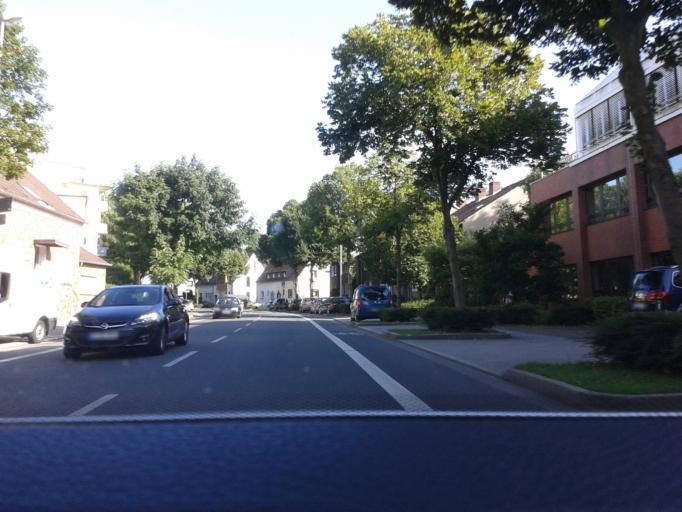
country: DE
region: North Rhine-Westphalia
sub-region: Regierungsbezirk Dusseldorf
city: Muelheim (Ruhr)
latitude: 51.4455
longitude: 6.8488
